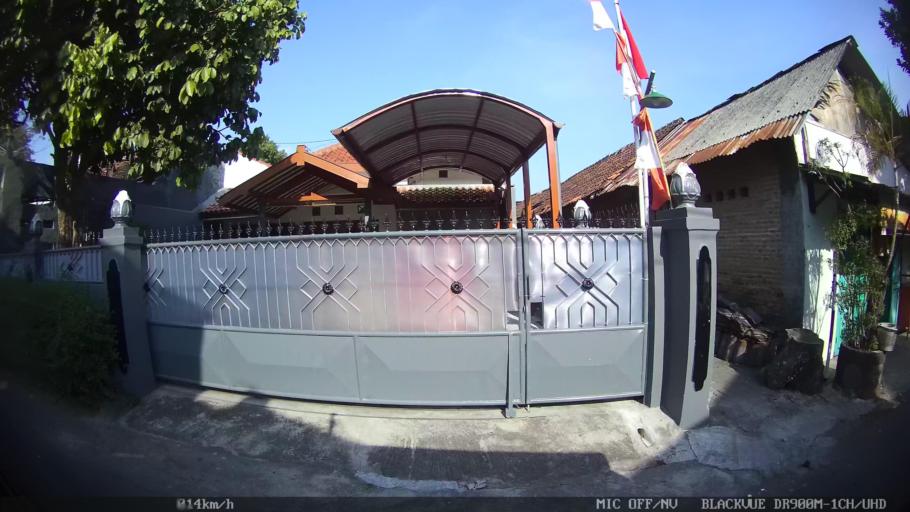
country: ID
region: Daerah Istimewa Yogyakarta
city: Yogyakarta
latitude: -7.8229
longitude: 110.3837
